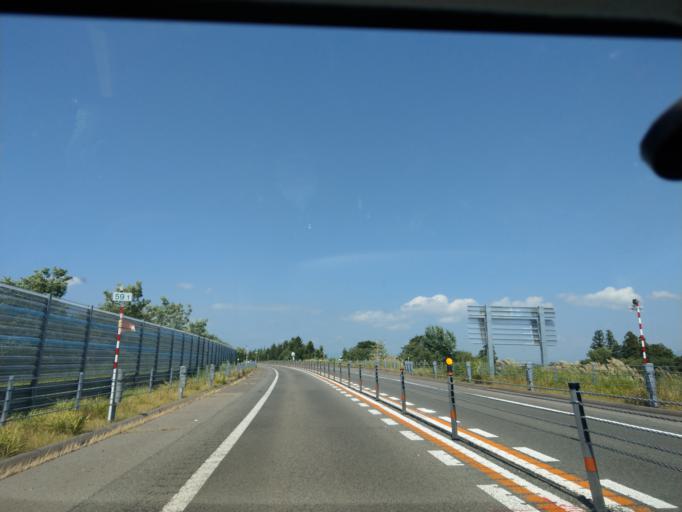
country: JP
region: Akita
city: Yokotemachi
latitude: 39.3415
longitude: 140.5010
